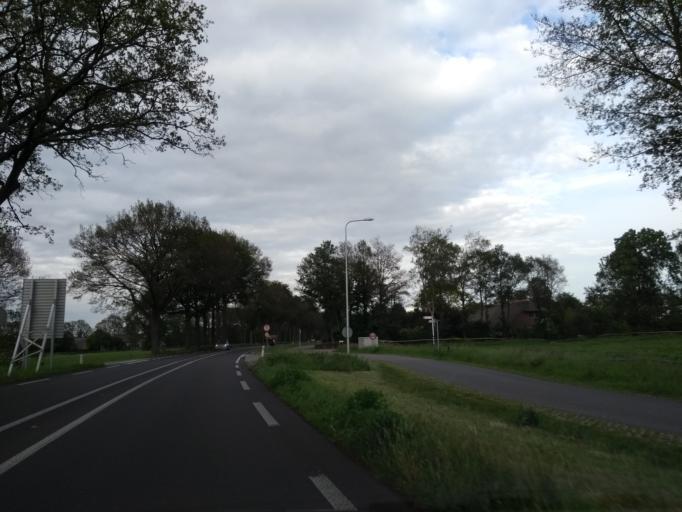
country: NL
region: Gelderland
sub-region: Berkelland
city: Borculo
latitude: 52.1211
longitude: 6.5491
